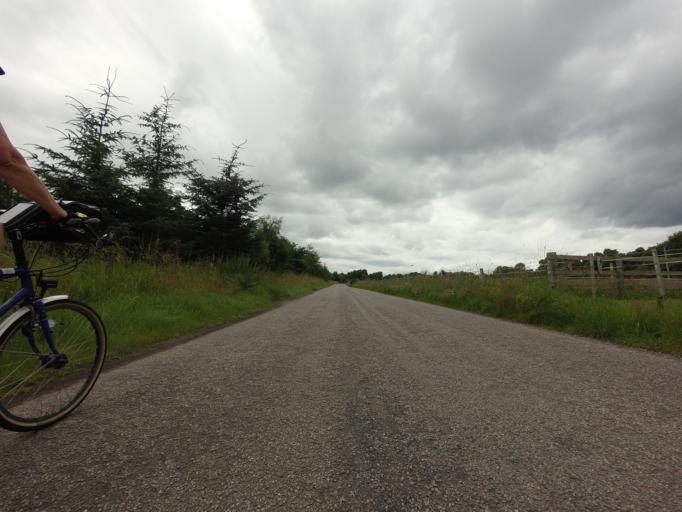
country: GB
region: Scotland
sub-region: Highland
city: Nairn
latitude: 57.5994
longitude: -3.7994
